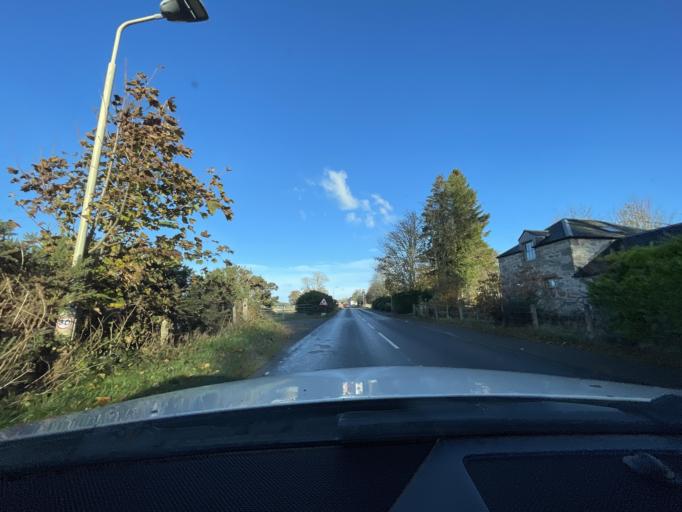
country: GB
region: Scotland
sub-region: Highland
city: Inverness
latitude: 57.3834
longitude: -4.3310
